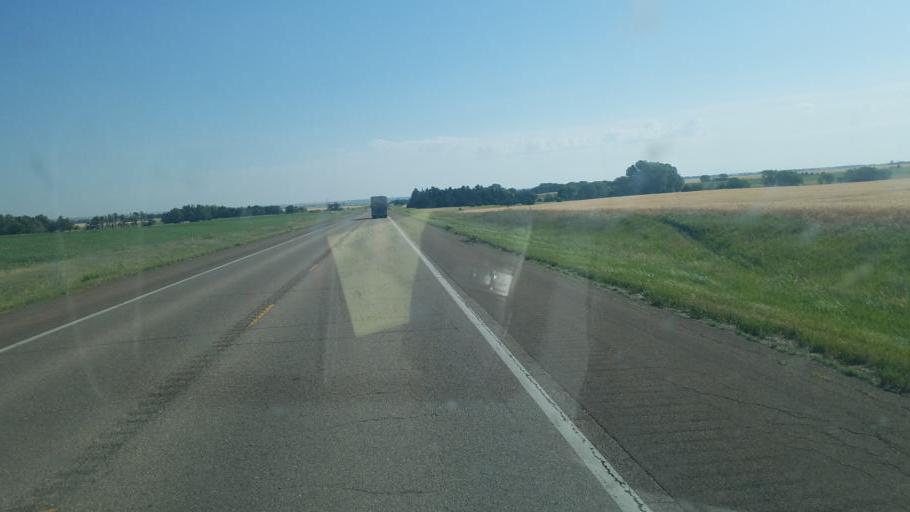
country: US
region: Kansas
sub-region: Barton County
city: Ellinwood
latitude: 38.3997
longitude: -98.6700
